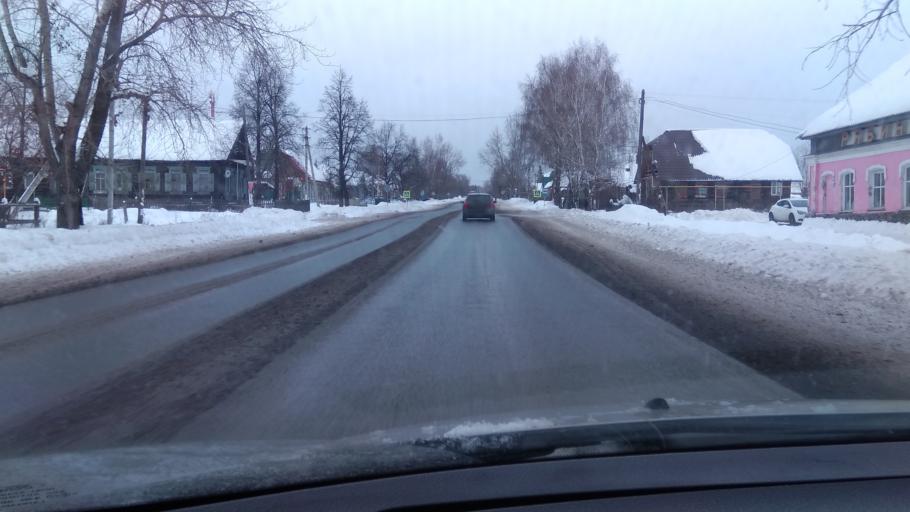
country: RU
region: Sverdlovsk
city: Nikolo-Pavlovskoye
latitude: 57.7870
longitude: 60.0553
